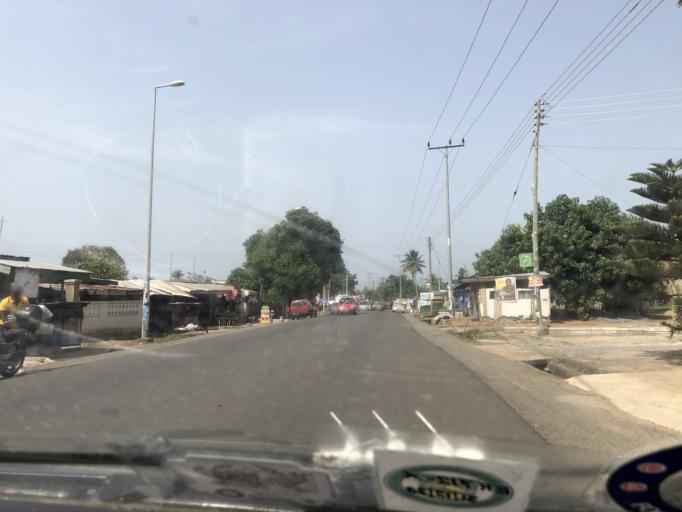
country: GH
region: Eastern
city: Koforidua
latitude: 6.0910
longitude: -0.2719
